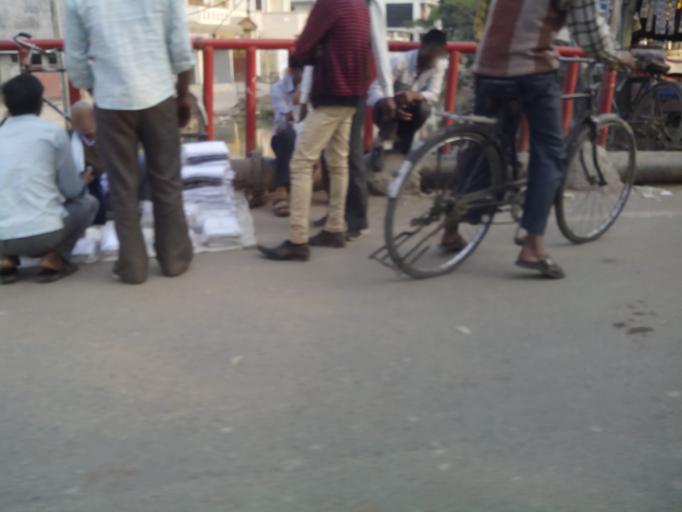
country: IN
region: Uttar Pradesh
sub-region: Kanpur
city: Kanpur
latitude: 26.4330
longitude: 80.3085
